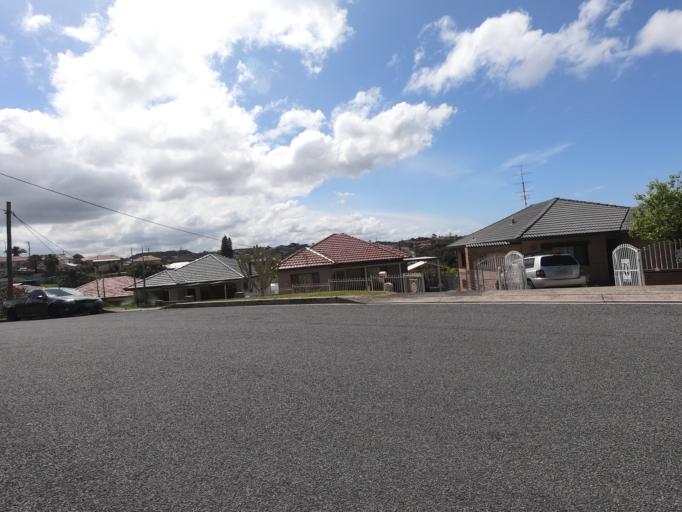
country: AU
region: New South Wales
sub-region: Wollongong
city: Lake Heights
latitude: -34.4880
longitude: 150.8703
